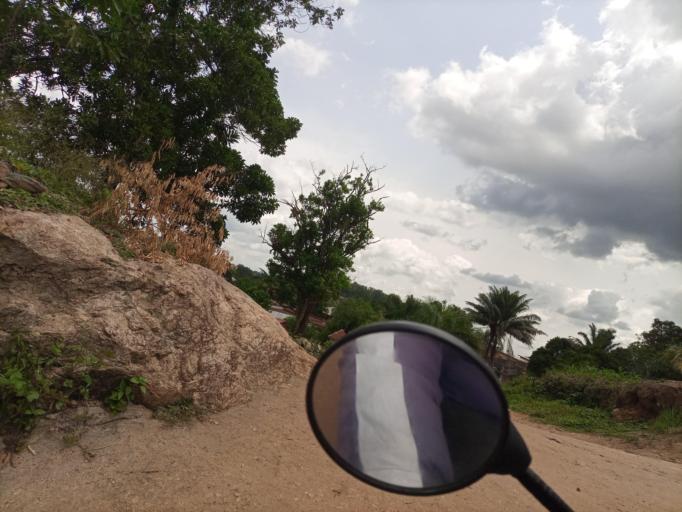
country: SL
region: Southern Province
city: Bo
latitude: 7.9500
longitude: -11.7380
